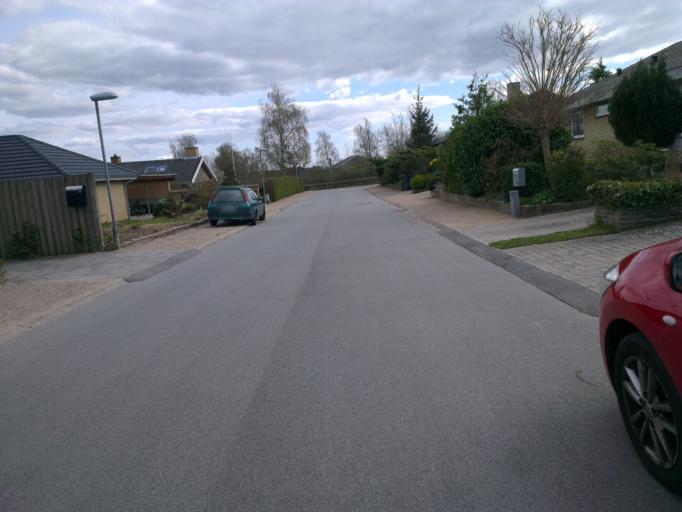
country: DK
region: Capital Region
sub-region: Frederikssund Kommune
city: Frederikssund
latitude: 55.8322
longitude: 12.0815
